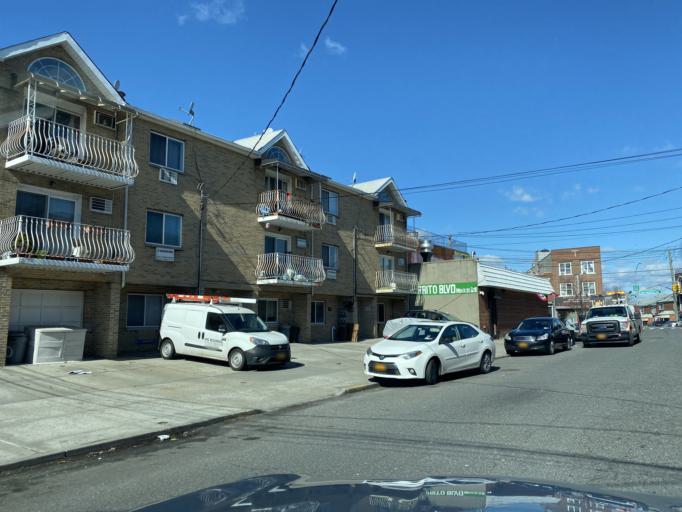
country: US
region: New York
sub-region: Kings County
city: East New York
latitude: 40.7121
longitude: -73.8792
